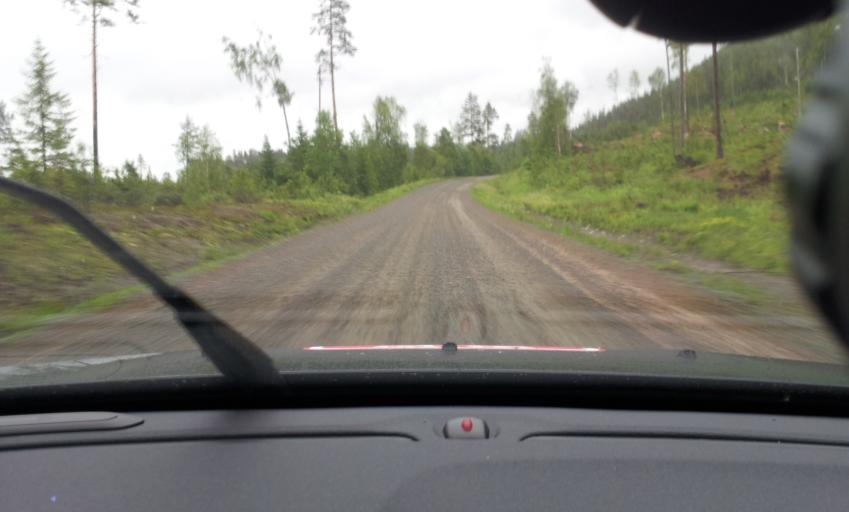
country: SE
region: Jaemtland
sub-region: Ragunda Kommun
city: Hammarstrand
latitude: 63.1352
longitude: 16.0904
